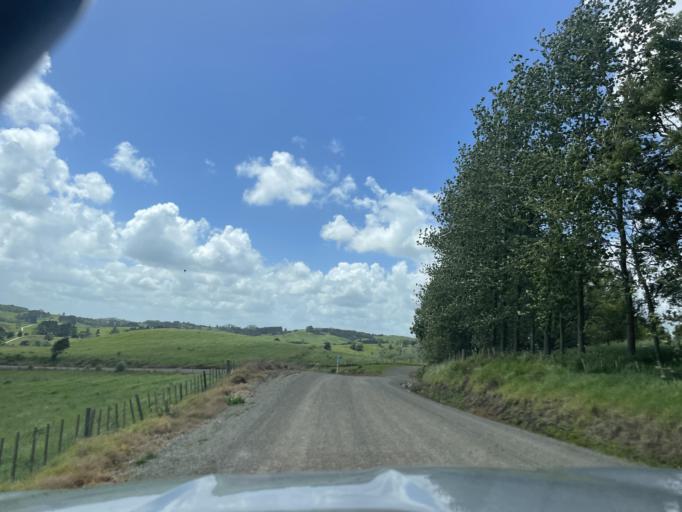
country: NZ
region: Auckland
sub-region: Auckland
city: Wellsford
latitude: -36.1664
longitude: 174.3208
